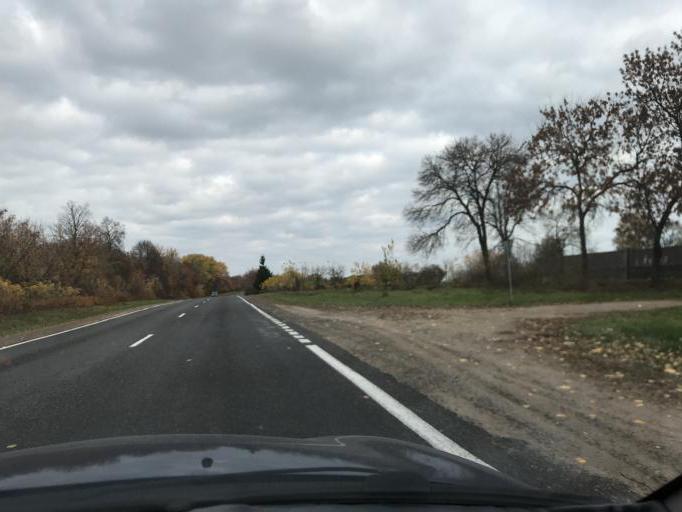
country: BY
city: Berezovka
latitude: 53.7415
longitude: 25.3749
